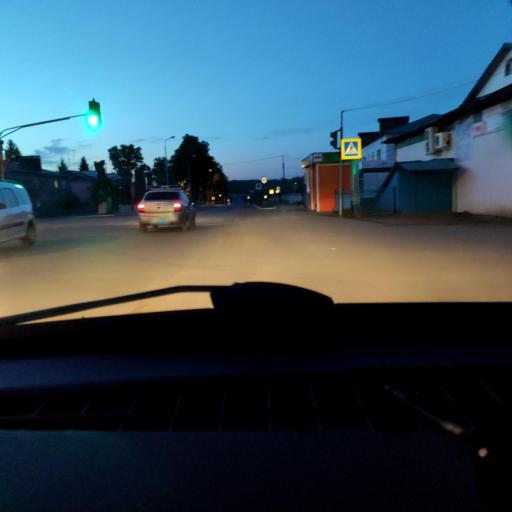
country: RU
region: Bashkortostan
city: Karmaskaly
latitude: 54.3704
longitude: 56.1708
